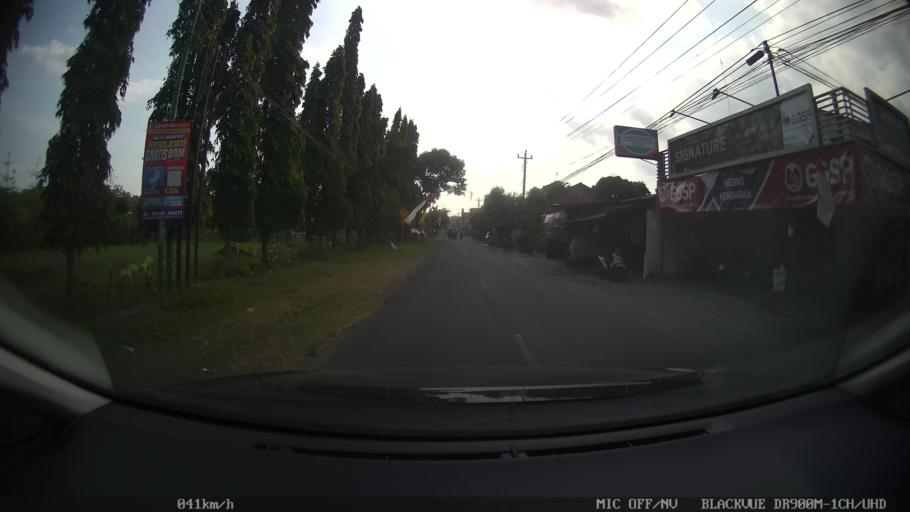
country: ID
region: Daerah Istimewa Yogyakarta
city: Kasihan
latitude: -7.8294
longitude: 110.3365
